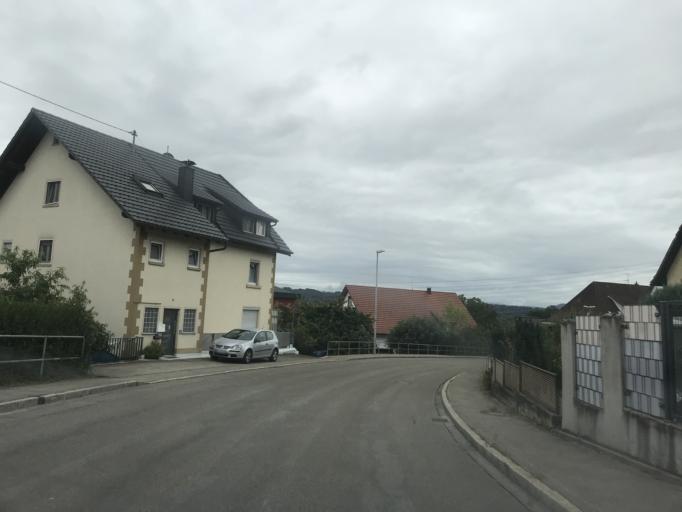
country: DE
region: Baden-Wuerttemberg
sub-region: Freiburg Region
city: Murg
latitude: 47.5653
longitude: 8.0337
